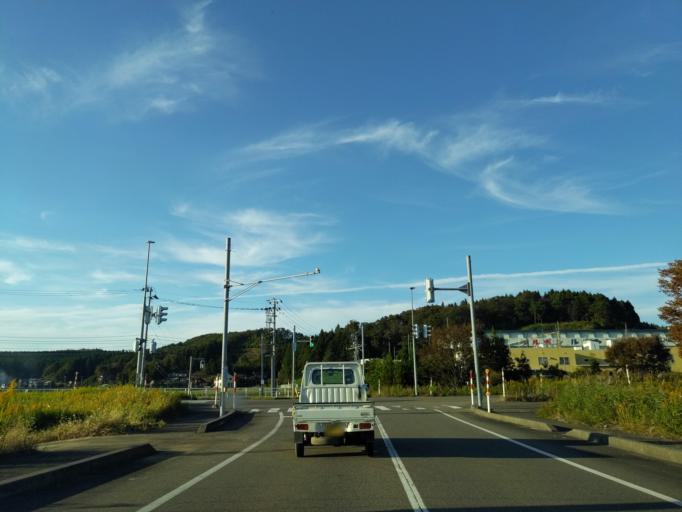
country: JP
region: Niigata
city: Nagaoka
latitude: 37.5774
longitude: 138.7531
